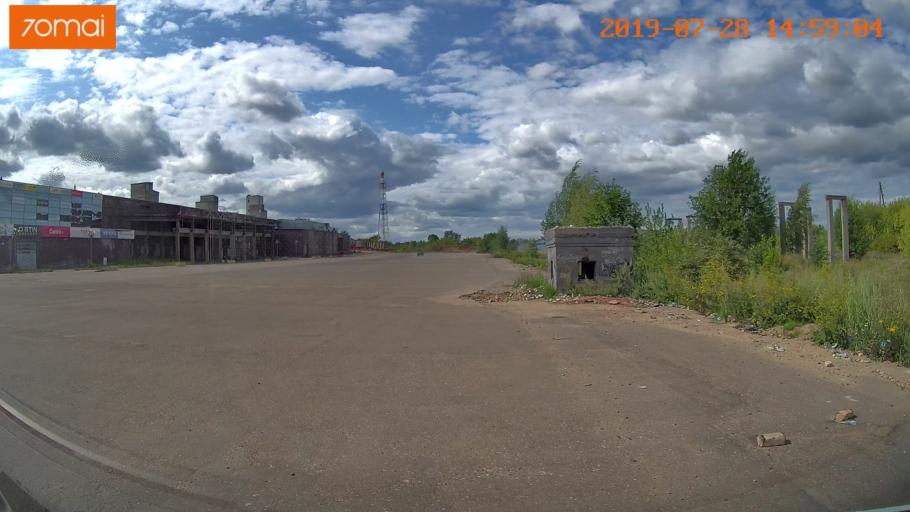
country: RU
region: Ivanovo
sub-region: Gorod Ivanovo
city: Ivanovo
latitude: 56.9666
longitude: 41.0263
